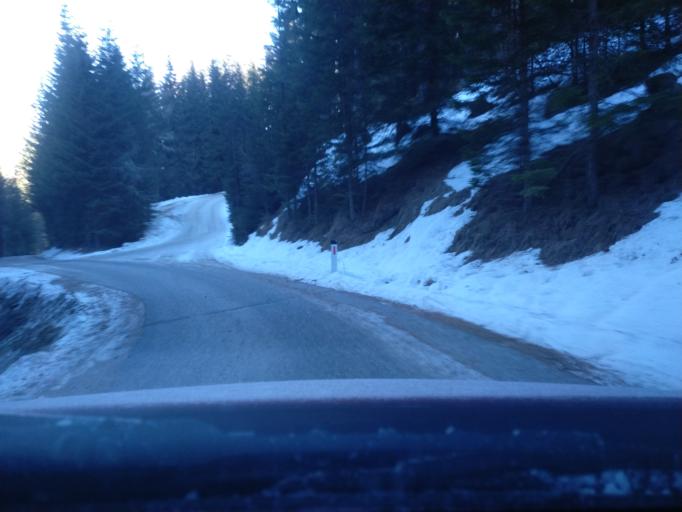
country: AT
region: Carinthia
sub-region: Politischer Bezirk Villach Land
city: Arriach
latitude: 46.7056
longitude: 13.9011
